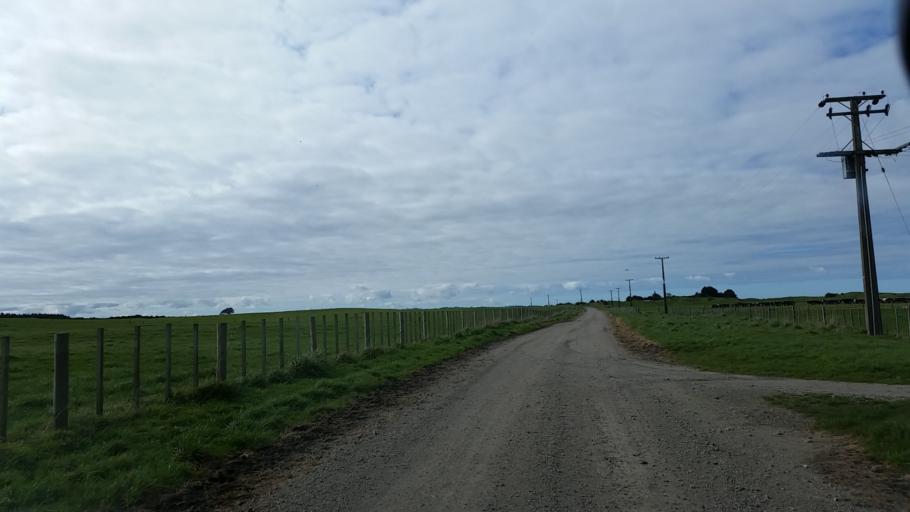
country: NZ
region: Taranaki
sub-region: South Taranaki District
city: Patea
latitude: -39.8070
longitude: 174.6503
